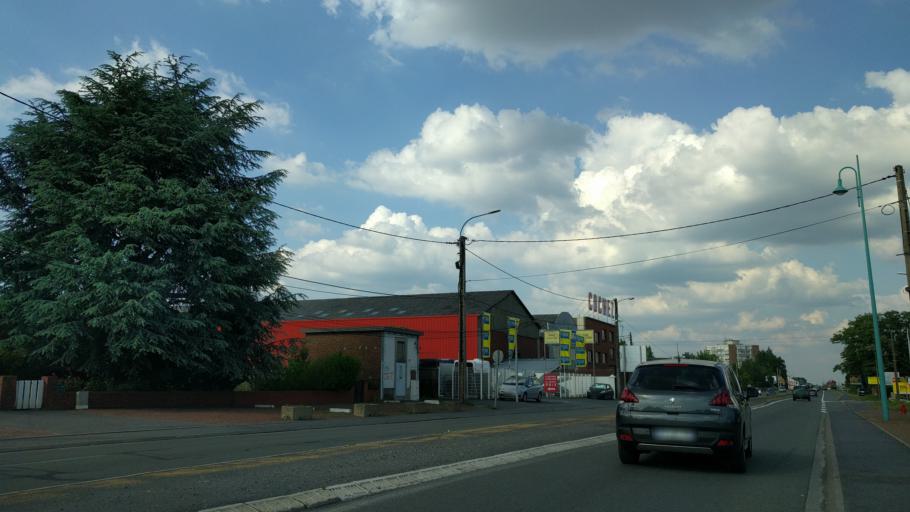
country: FR
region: Nord-Pas-de-Calais
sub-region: Departement du Nord
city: La Sentinelle
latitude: 50.3447
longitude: 3.4789
